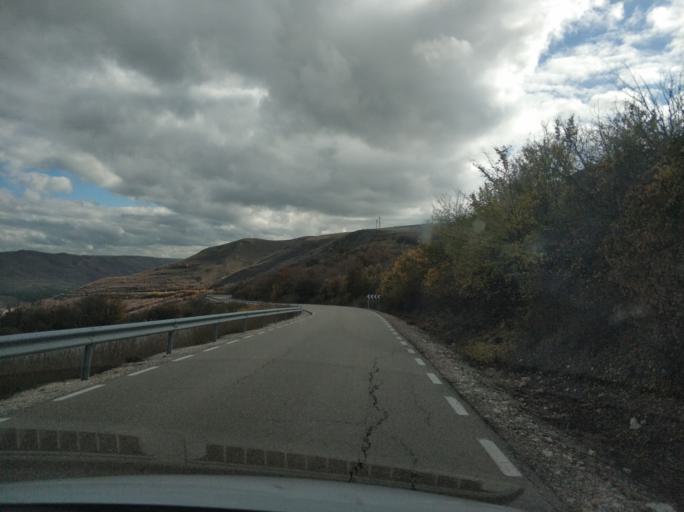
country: ES
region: Castille and Leon
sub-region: Provincia de Soria
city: Medinaceli
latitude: 41.1665
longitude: -2.4354
